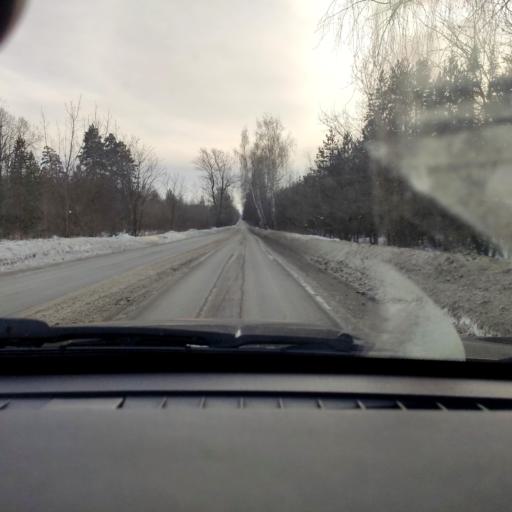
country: RU
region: Samara
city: Pribrezhnyy
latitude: 53.5132
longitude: 49.8510
